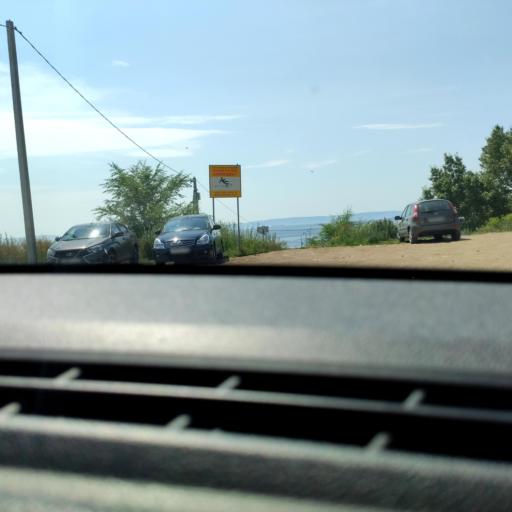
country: RU
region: Samara
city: Podstepki
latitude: 53.5102
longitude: 49.2254
